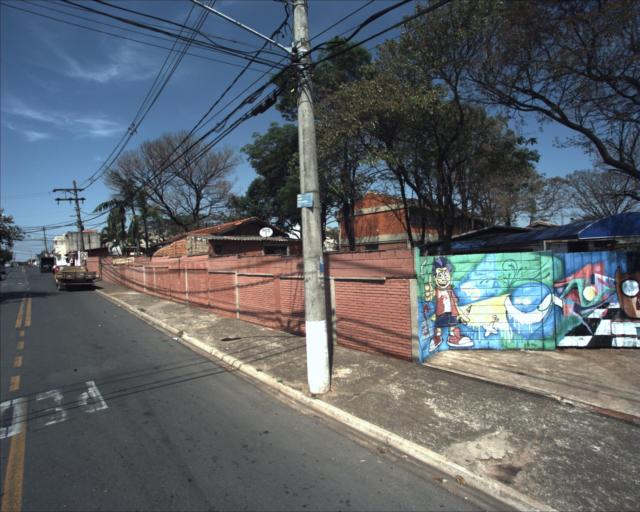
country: BR
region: Sao Paulo
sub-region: Sorocaba
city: Sorocaba
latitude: -23.4599
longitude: -47.4938
